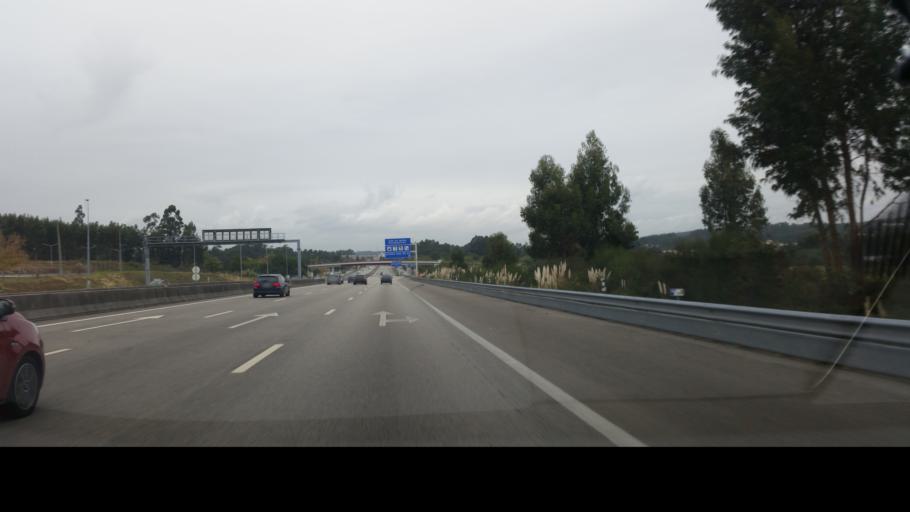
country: PT
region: Porto
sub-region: Maia
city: Nogueira
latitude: 41.2584
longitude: -8.5667
